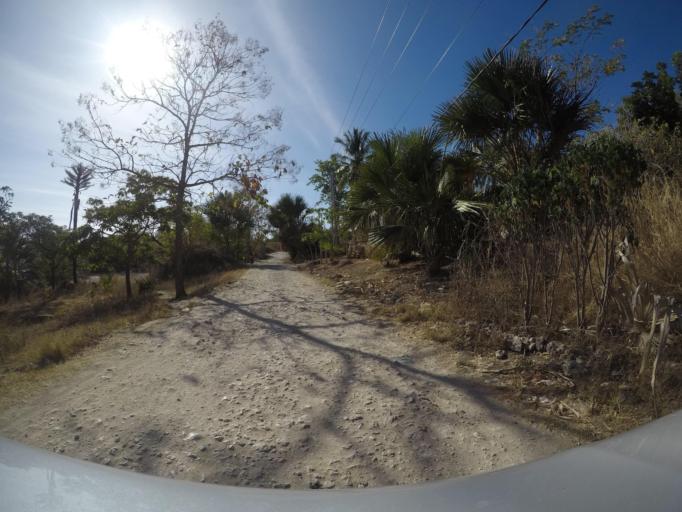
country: TL
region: Baucau
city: Baucau
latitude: -8.4546
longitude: 126.4409
